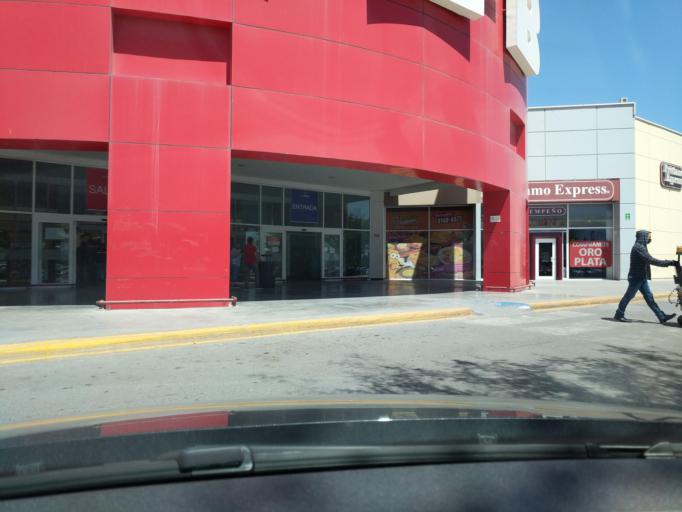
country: MX
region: Nuevo Leon
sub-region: Apodaca
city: Fraccionamiento Cosmopolis Octavo Sector
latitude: 25.7851
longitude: -100.2266
